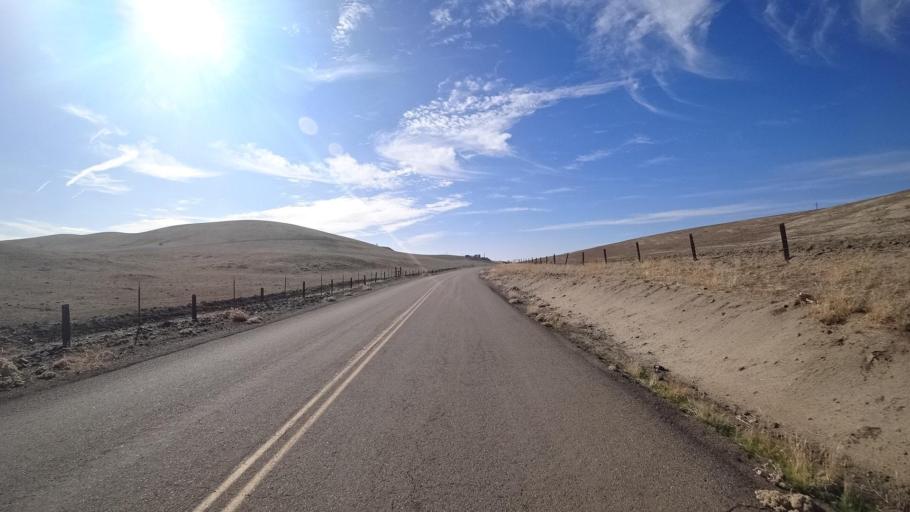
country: US
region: California
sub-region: Tulare County
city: Richgrove
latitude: 35.6352
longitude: -118.9510
